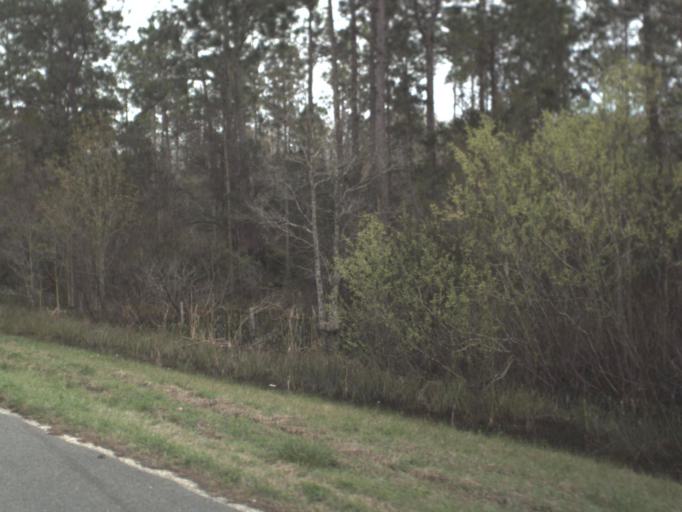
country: US
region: Florida
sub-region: Leon County
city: Woodville
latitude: 30.1910
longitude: -84.0740
